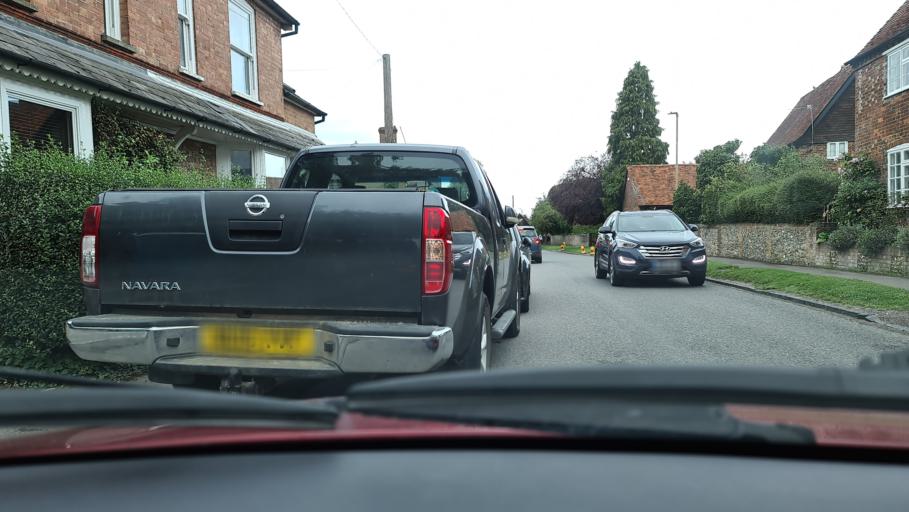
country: GB
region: England
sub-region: Oxfordshire
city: Chinnor
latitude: 51.7041
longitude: -0.9062
